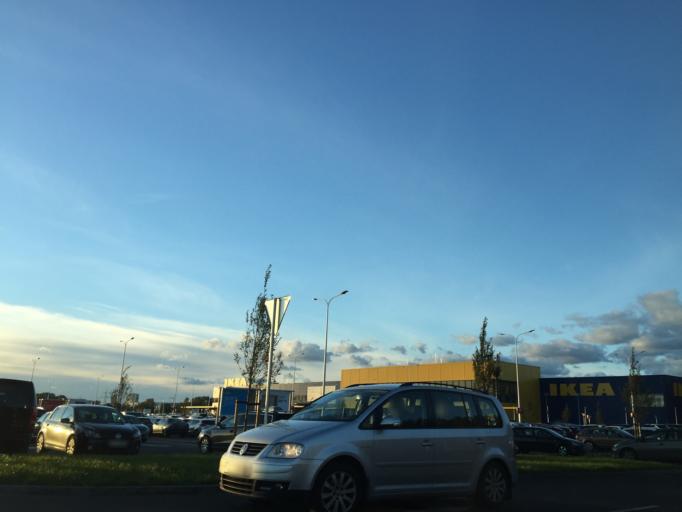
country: LV
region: Stopini
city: Ulbroka
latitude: 56.9529
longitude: 24.2570
